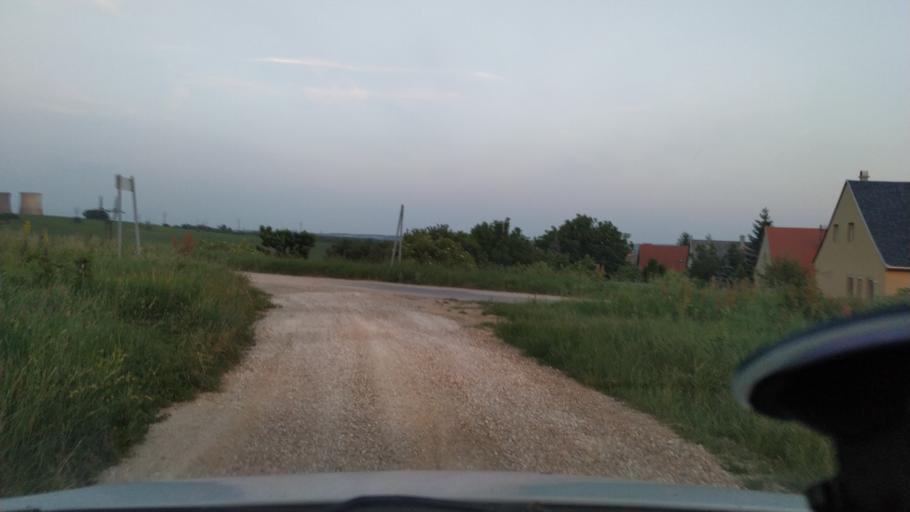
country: HU
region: Veszprem
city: Varpalota
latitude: 47.2036
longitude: 18.1834
